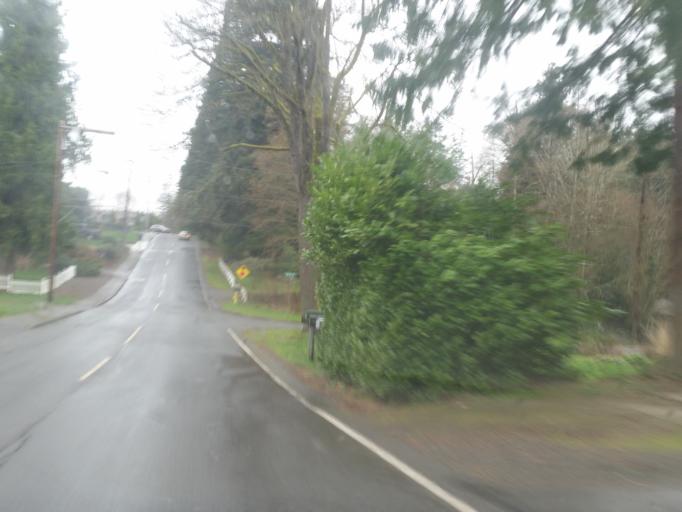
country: US
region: Washington
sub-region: Snohomish County
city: Edmonds
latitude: 47.8179
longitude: -122.3529
